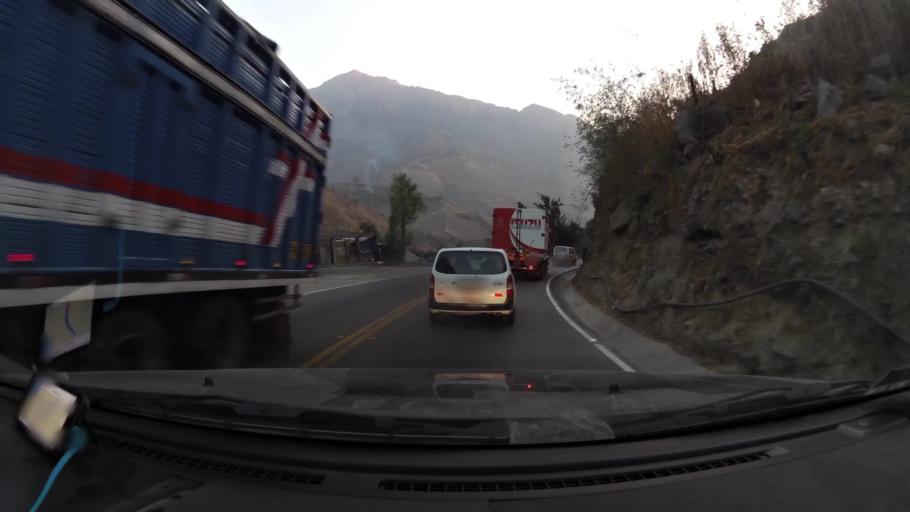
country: PE
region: Lima
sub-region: Provincia de Huarochiri
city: Surco
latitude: -11.8766
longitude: -76.4305
